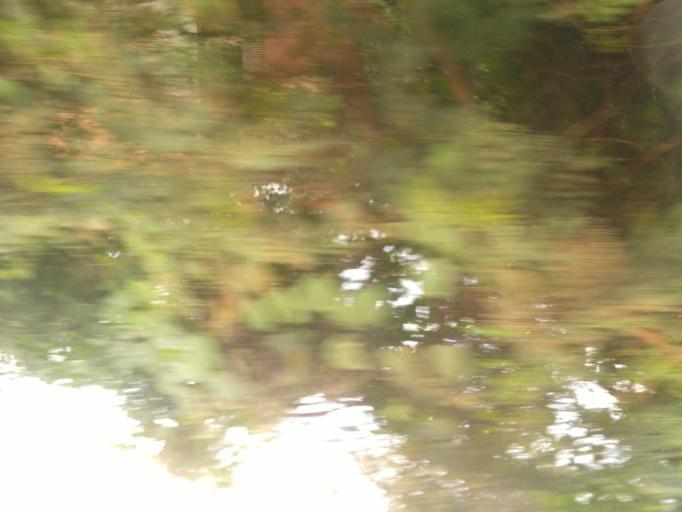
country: UG
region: Central Region
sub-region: Wakiso District
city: Kireka
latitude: 0.3693
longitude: 32.6129
